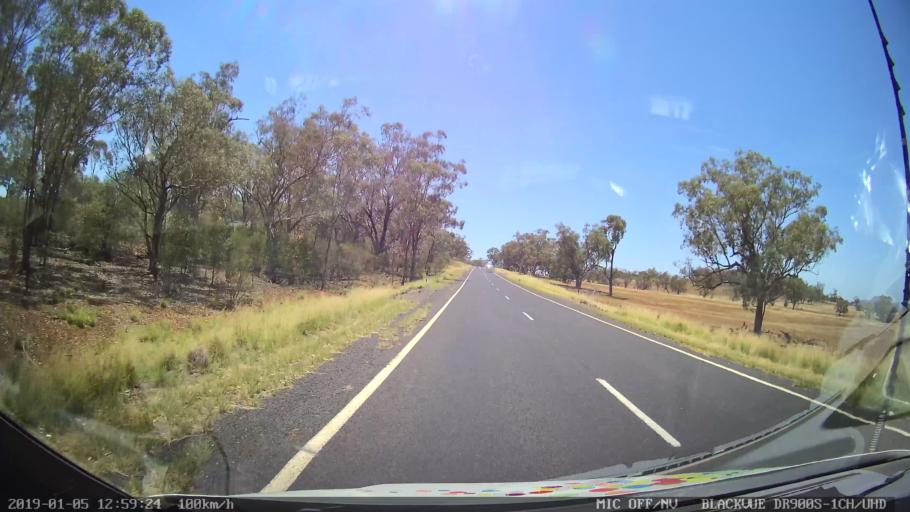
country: AU
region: New South Wales
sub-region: Narrabri
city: Boggabri
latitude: -31.1131
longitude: 149.7653
